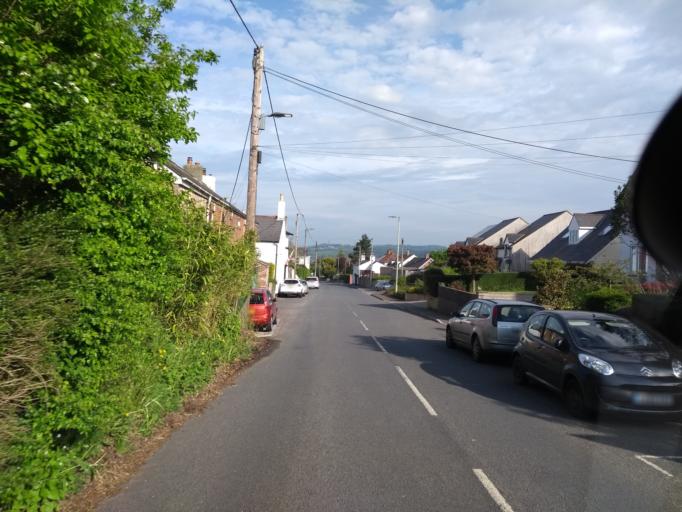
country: GB
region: England
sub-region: Devon
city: Axminster
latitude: 50.7780
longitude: -2.9861
